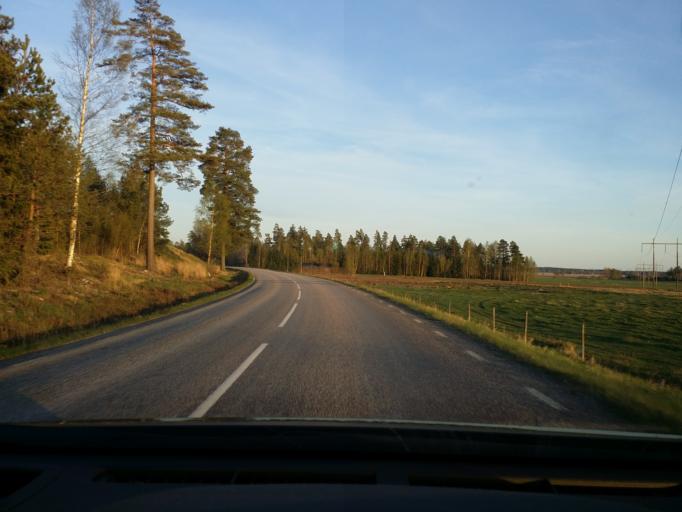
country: SE
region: Vaestmanland
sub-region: Sala Kommun
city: Sala
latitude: 59.8184
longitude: 16.5308
